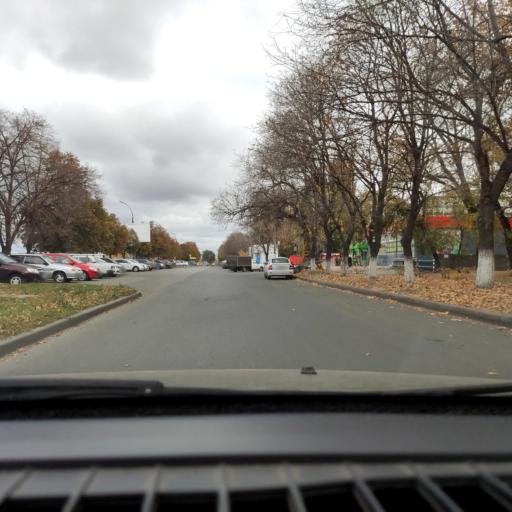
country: RU
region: Samara
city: Tol'yatti
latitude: 53.5356
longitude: 49.2634
